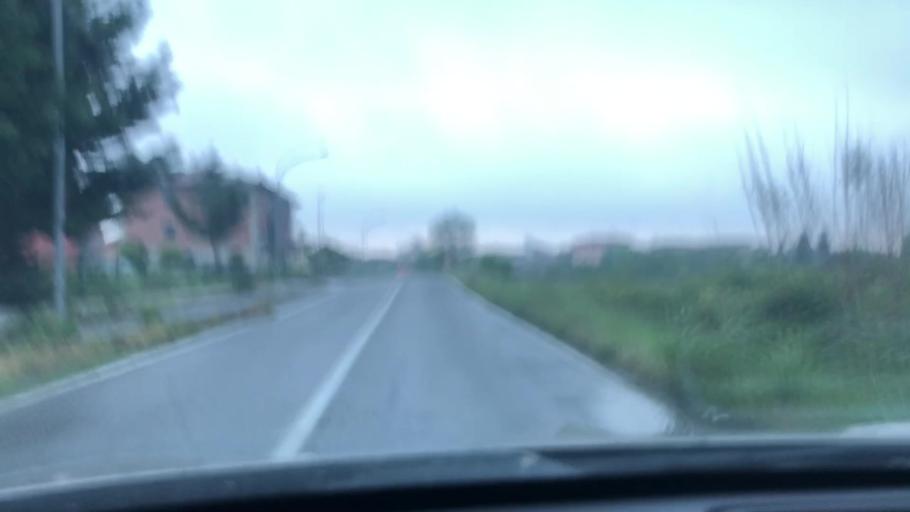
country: IT
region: Tuscany
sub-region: Province of Pisa
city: Val di Cava
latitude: 43.6438
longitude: 10.6484
